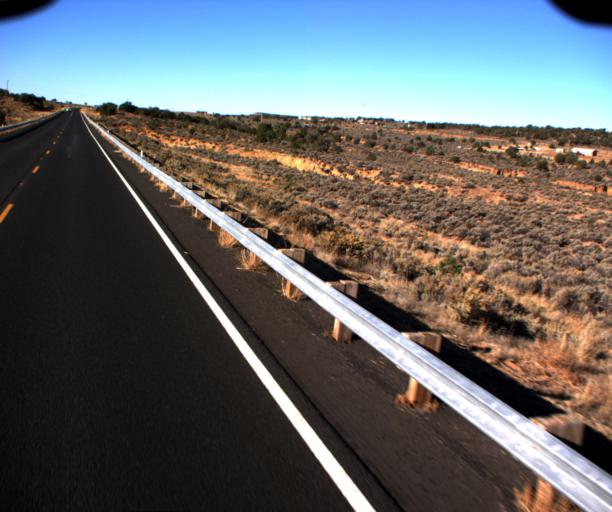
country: US
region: Arizona
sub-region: Apache County
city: Ganado
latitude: 35.7642
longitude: -109.7504
